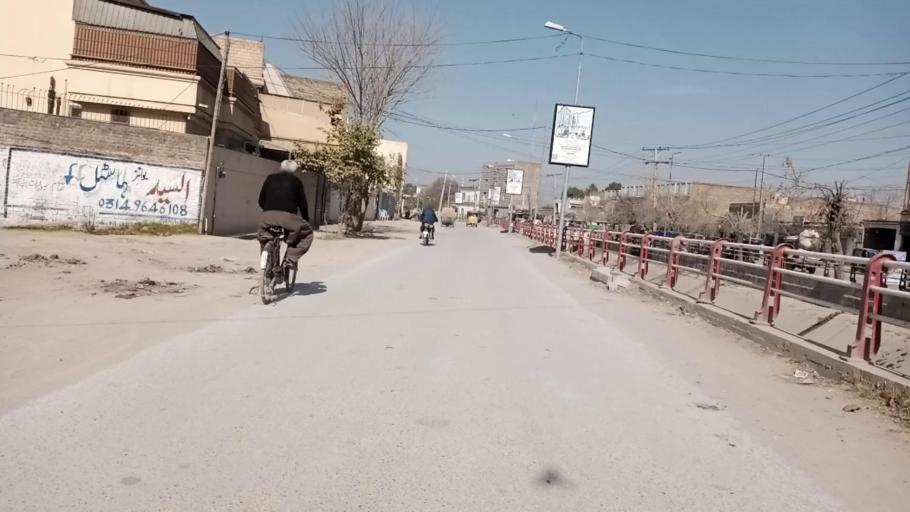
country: PK
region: Khyber Pakhtunkhwa
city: Peshawar
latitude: 33.9864
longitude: 71.4978
